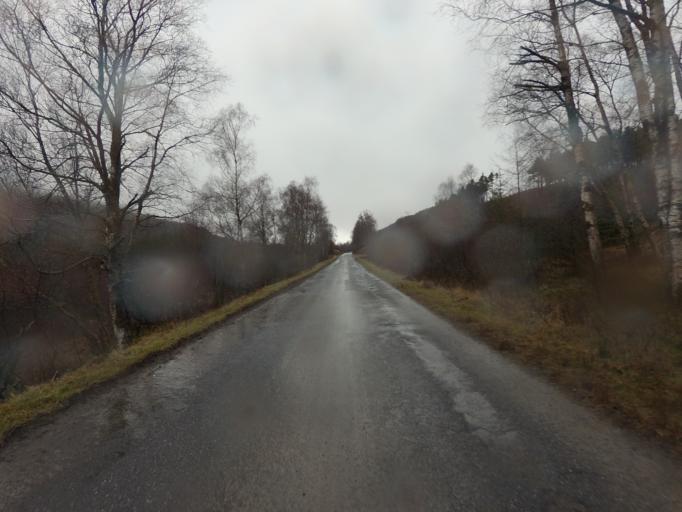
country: GB
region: Scotland
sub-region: West Dunbartonshire
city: Balloch
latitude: 56.2376
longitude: -4.5640
